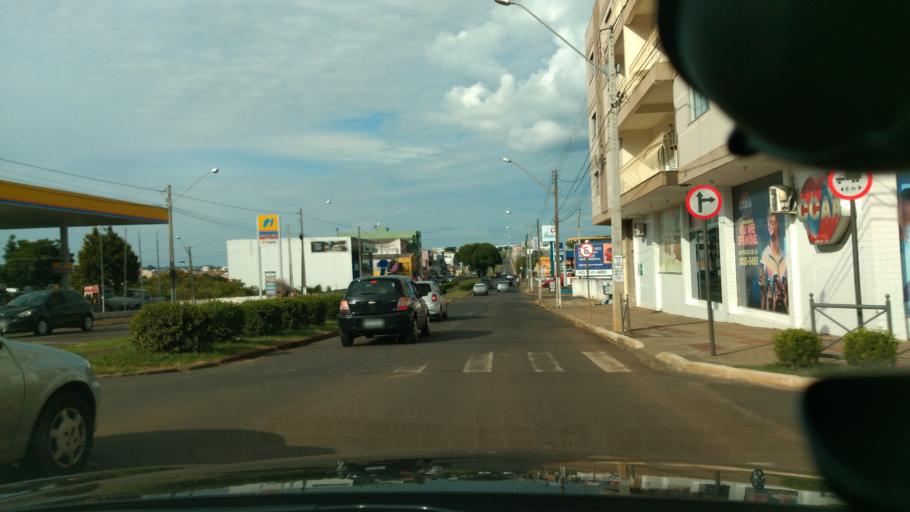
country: BR
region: Parana
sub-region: Guarapuava
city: Guarapuava
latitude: -25.3890
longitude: -51.4760
